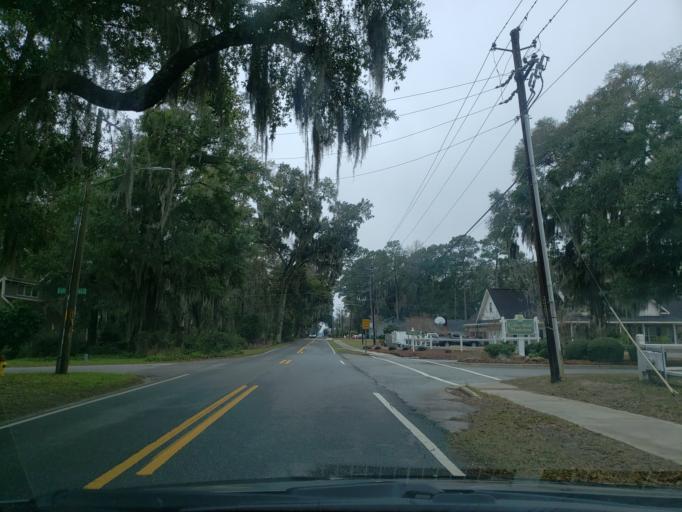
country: US
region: Georgia
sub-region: Chatham County
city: Montgomery
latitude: 31.9399
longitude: -81.1510
